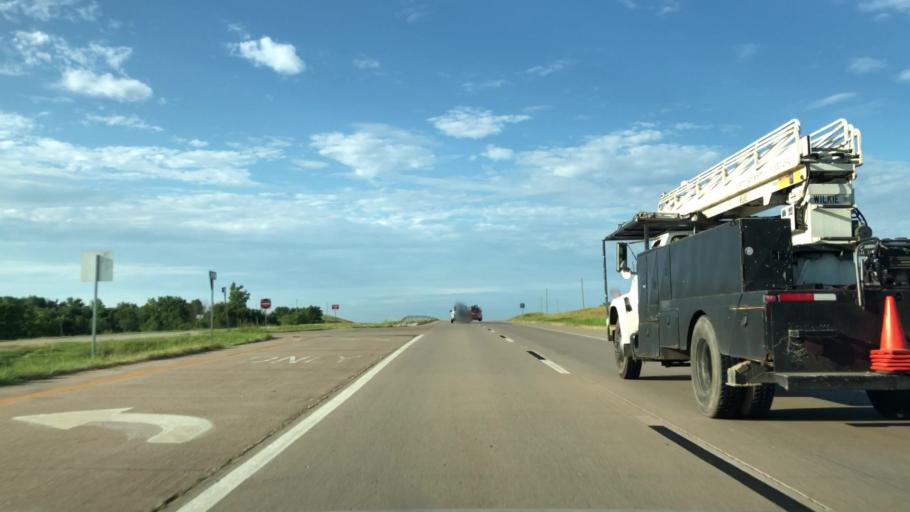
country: US
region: Oklahoma
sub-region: Osage County
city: Skiatook
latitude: 36.4820
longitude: -95.9207
